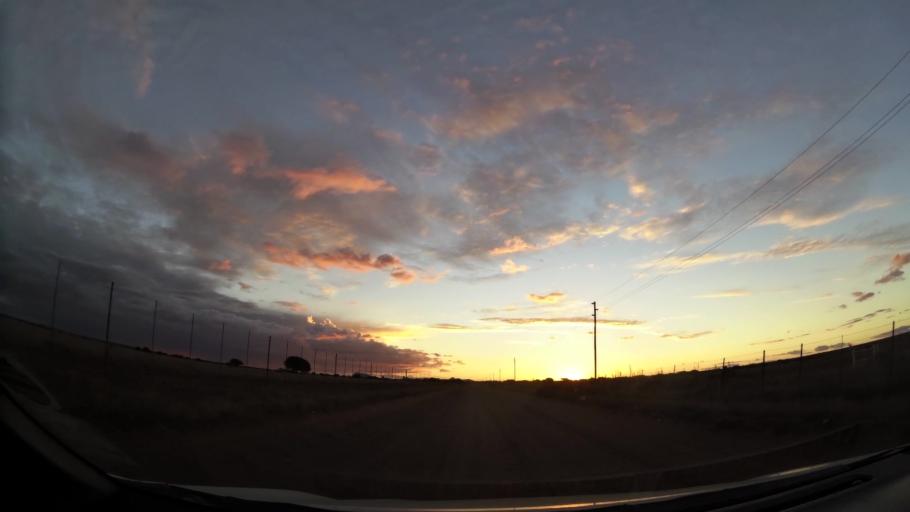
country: ZA
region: Limpopo
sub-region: Capricorn District Municipality
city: Polokwane
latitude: -23.7382
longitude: 29.4439
